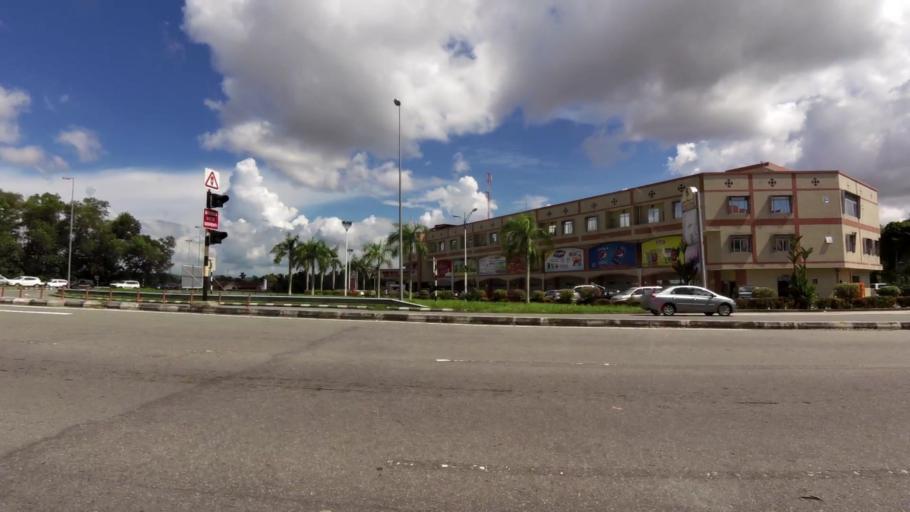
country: BN
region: Brunei and Muara
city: Bandar Seri Begawan
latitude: 4.9632
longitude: 114.9512
